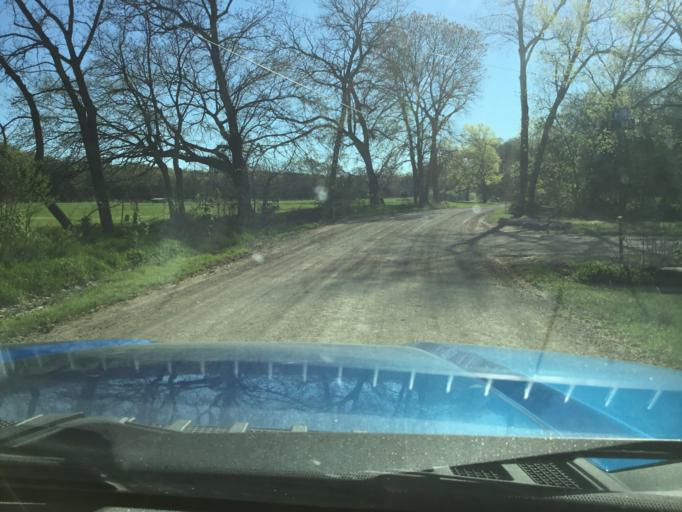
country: US
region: Kansas
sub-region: Douglas County
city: Lawrence
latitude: 38.9936
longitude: -95.3274
